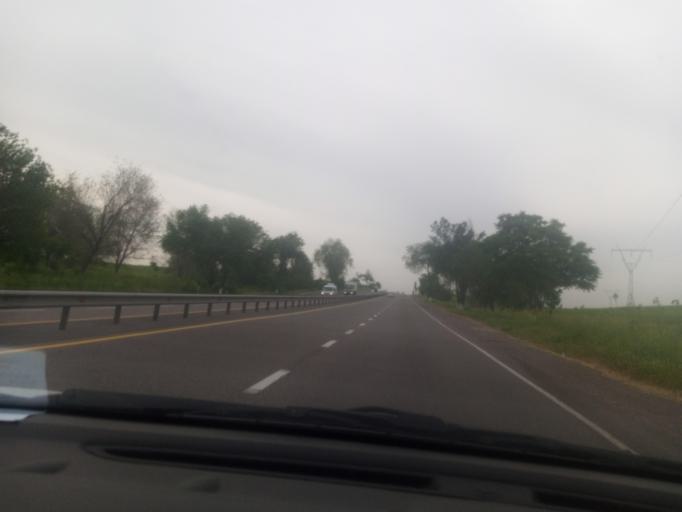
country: UZ
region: Toshkent
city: Tuytepa
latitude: 41.0668
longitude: 69.4797
